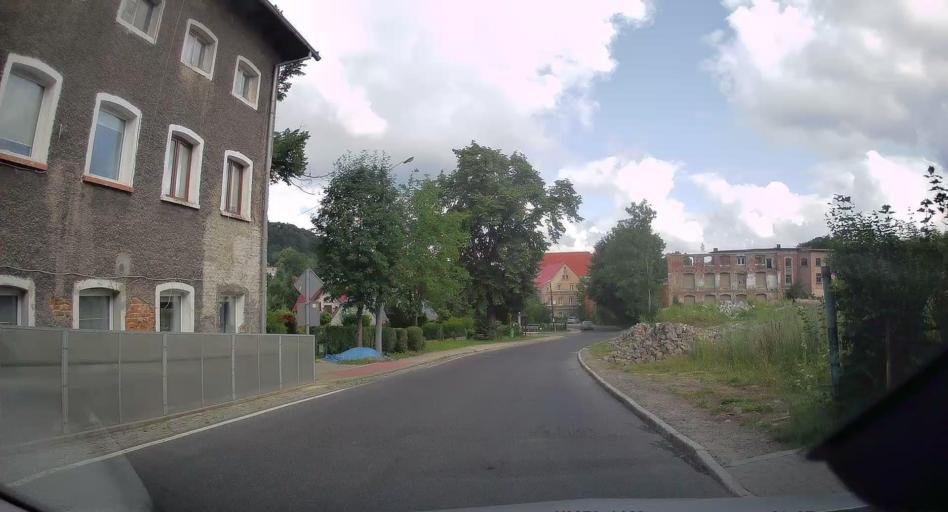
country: PL
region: Lower Silesian Voivodeship
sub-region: Powiat walbrzyski
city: Walim
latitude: 50.6950
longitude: 16.4447
